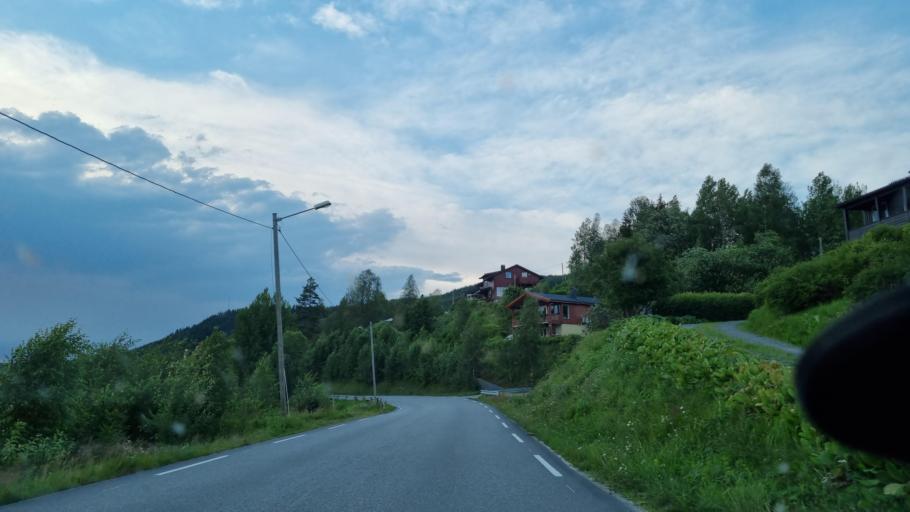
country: NO
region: Hedmark
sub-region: Trysil
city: Innbygda
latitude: 61.3203
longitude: 12.2597
